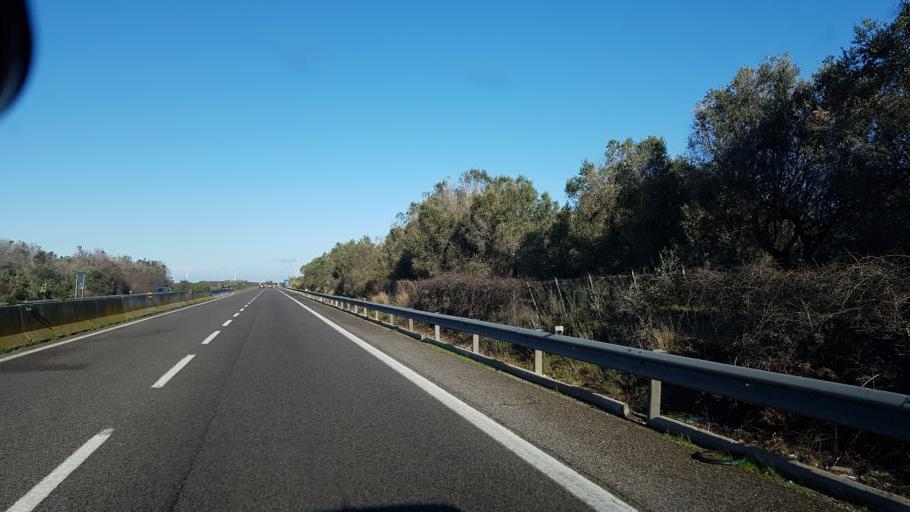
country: IT
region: Apulia
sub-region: Provincia di Brindisi
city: San Pietro Vernotico
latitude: 40.5360
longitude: 18.0067
